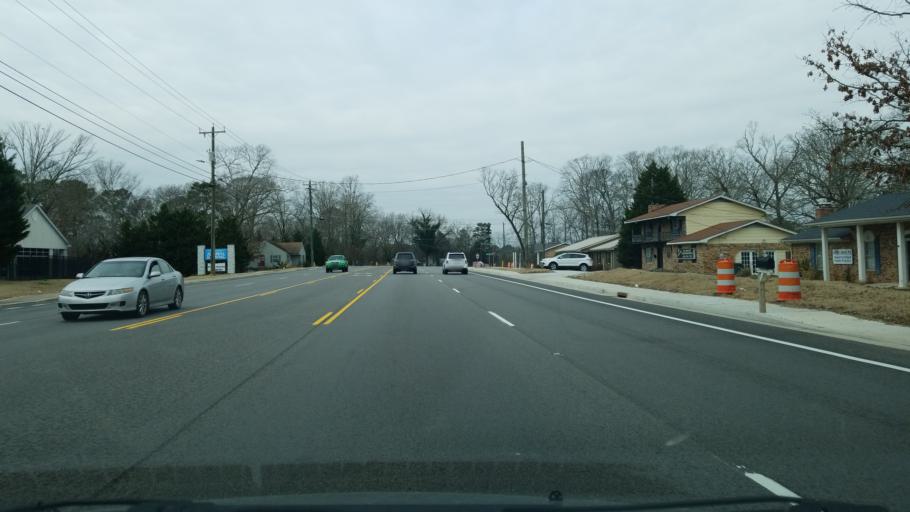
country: US
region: Tennessee
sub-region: Hamilton County
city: East Brainerd
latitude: 35.0016
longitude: -85.1373
